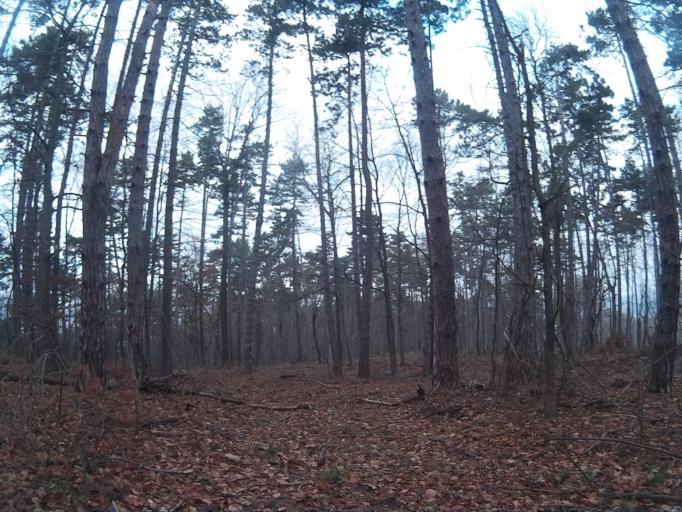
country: HU
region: Veszprem
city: Urkut
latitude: 47.1339
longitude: 17.6482
